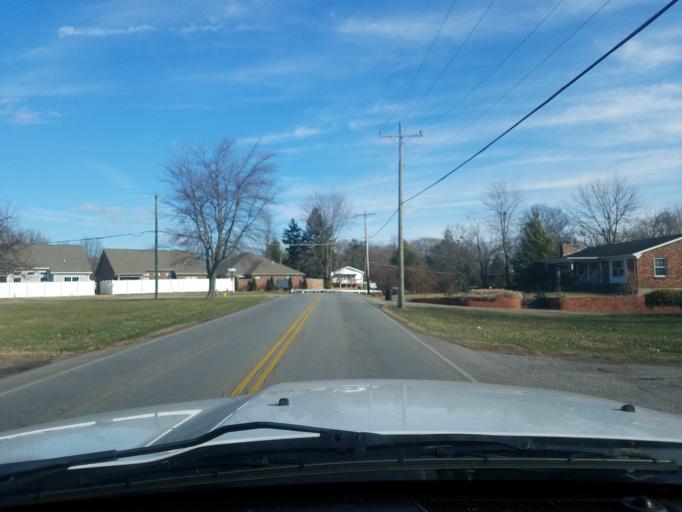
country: US
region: Indiana
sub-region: Clark County
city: Clarksville
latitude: 38.3159
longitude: -85.7745
